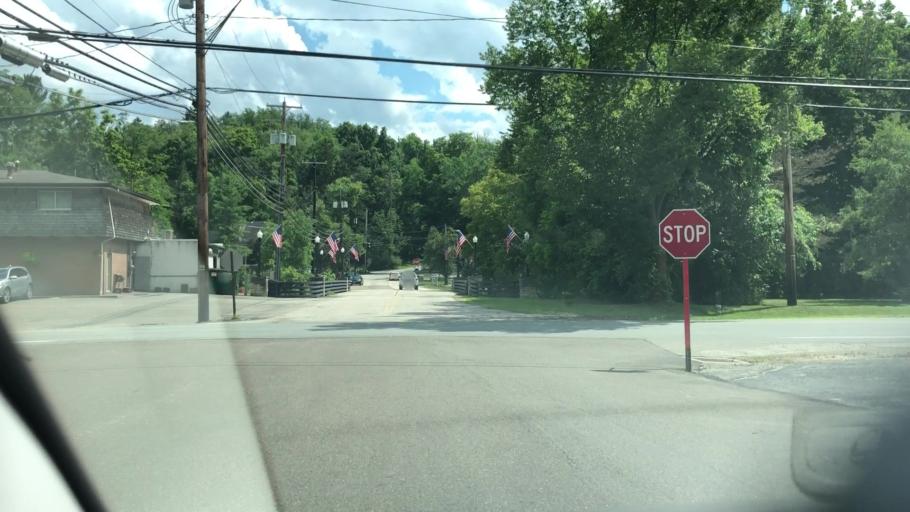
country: US
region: Ohio
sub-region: Summit County
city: Montrose-Ghent
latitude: 41.1584
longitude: -81.6370
